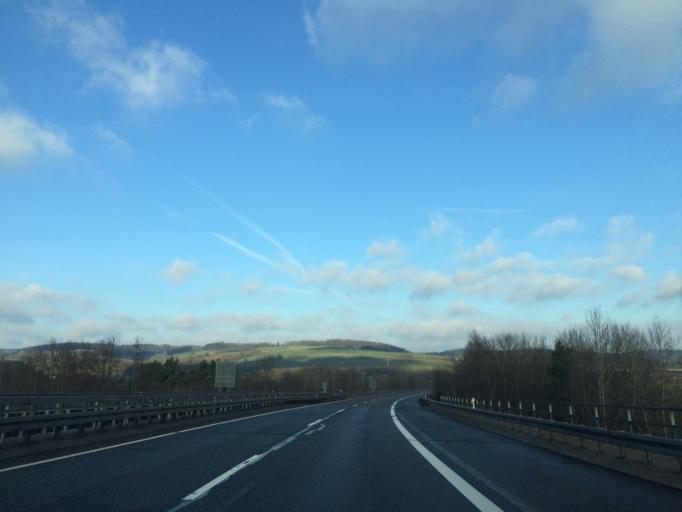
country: DE
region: Hesse
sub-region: Regierungsbezirk Kassel
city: Niederaula
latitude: 50.7667
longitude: 9.5900
